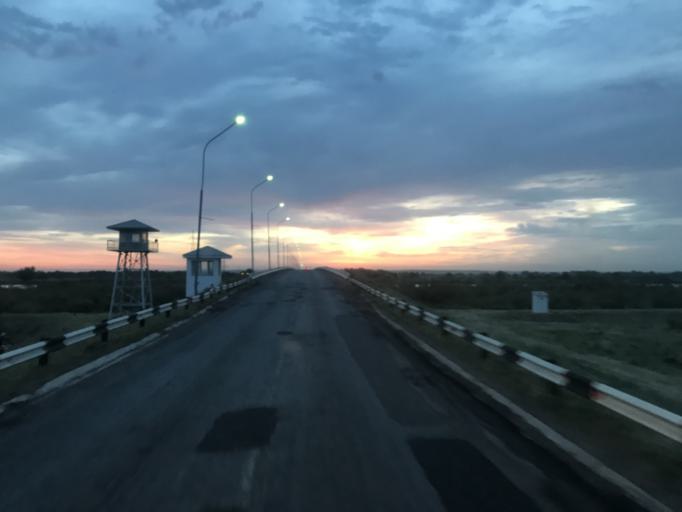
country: KZ
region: Ongtustik Qazaqstan
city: Ilyich
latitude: 41.0280
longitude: 68.5150
